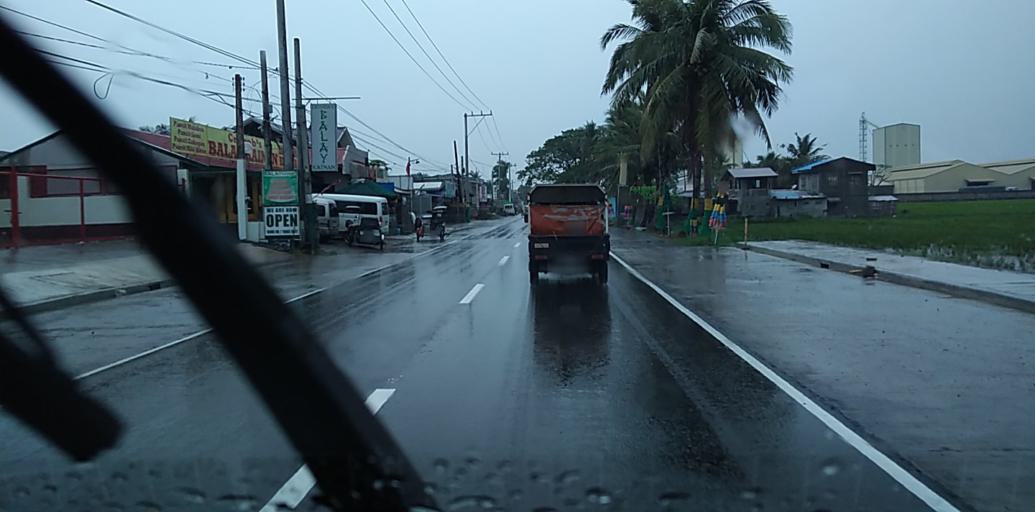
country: PH
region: Central Luzon
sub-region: Province of Bulacan
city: Bulualto
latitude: 15.2065
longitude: 120.9564
